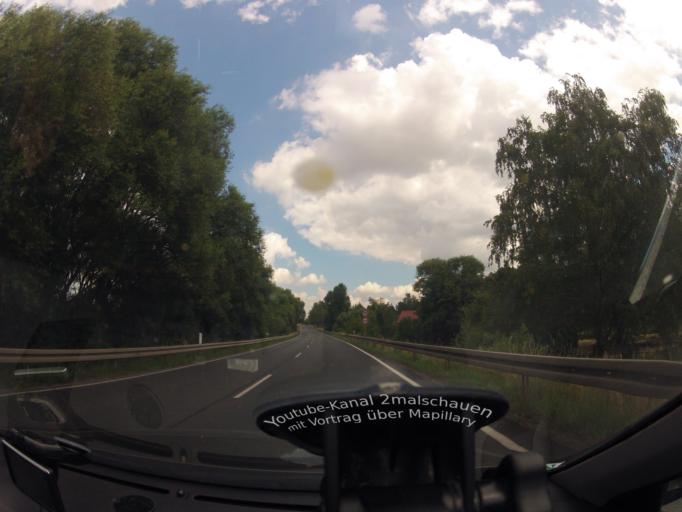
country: DE
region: Saxony
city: Taucha
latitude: 51.3853
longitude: 12.4995
